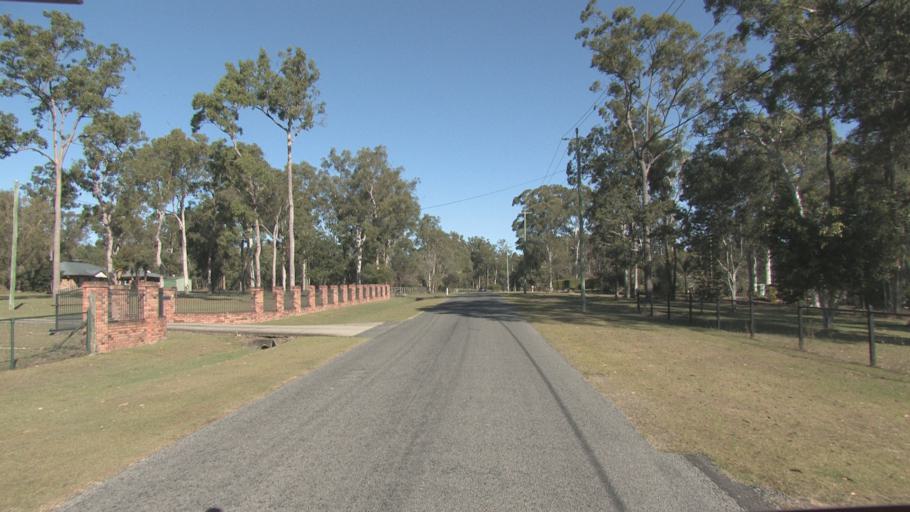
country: AU
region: Queensland
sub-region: Logan
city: Chambers Flat
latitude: -27.7380
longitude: 153.0707
